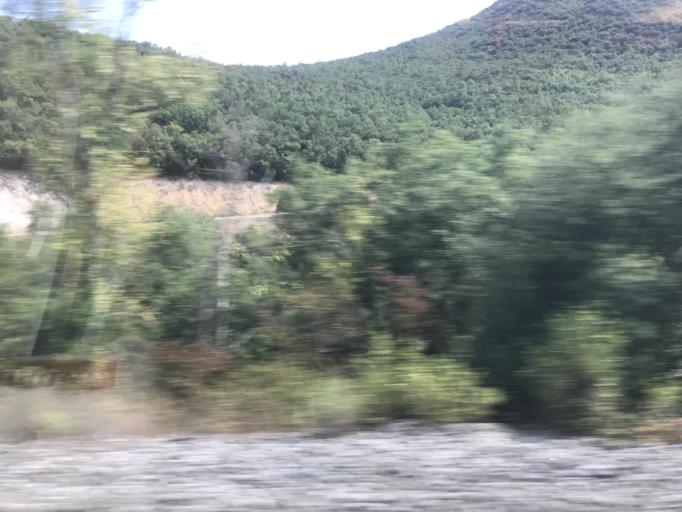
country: ES
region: Castille and Leon
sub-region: Provincia de Burgos
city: Bugedo
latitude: 42.6510
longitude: -3.0062
